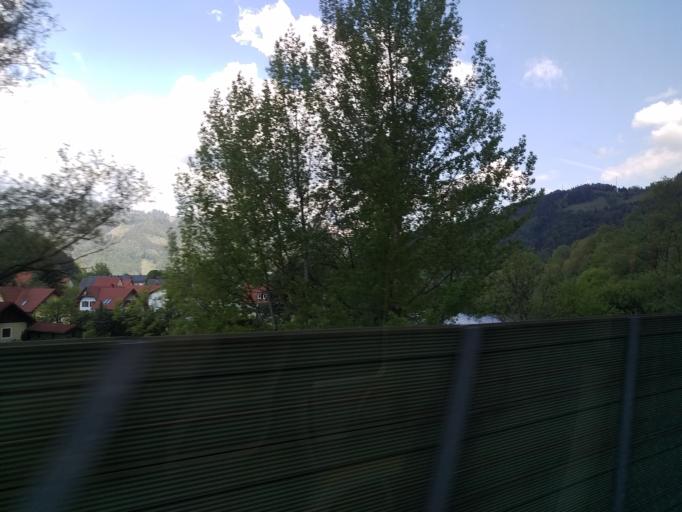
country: AT
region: Styria
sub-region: Politischer Bezirk Graz-Umgebung
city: Schrems bei Frohnleiten
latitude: 47.2734
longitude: 15.3335
